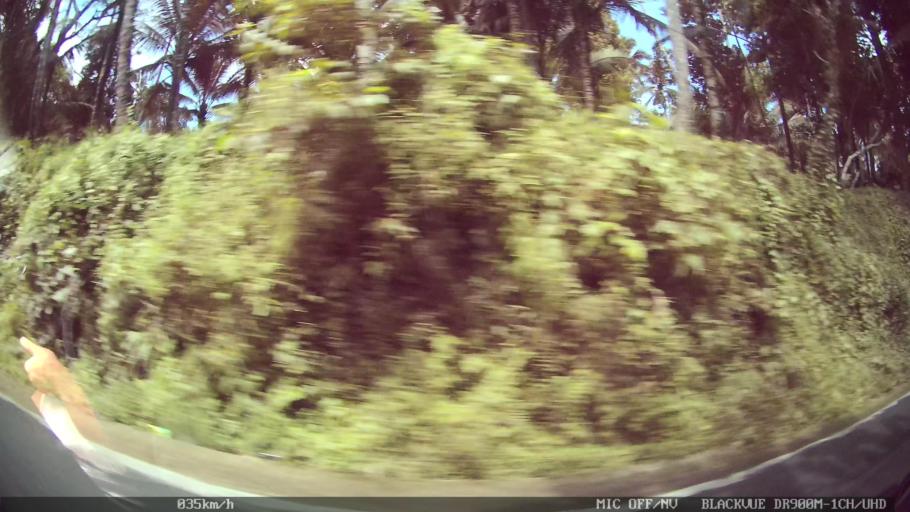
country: ID
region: Bali
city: Banjar Apuan Kaja
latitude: -8.5000
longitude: 115.3409
